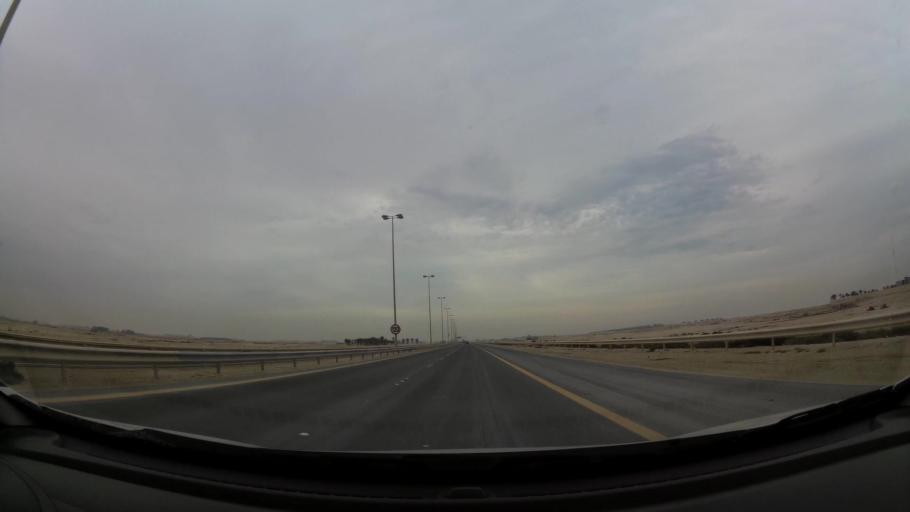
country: BH
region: Central Governorate
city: Dar Kulayb
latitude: 26.0274
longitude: 50.6077
